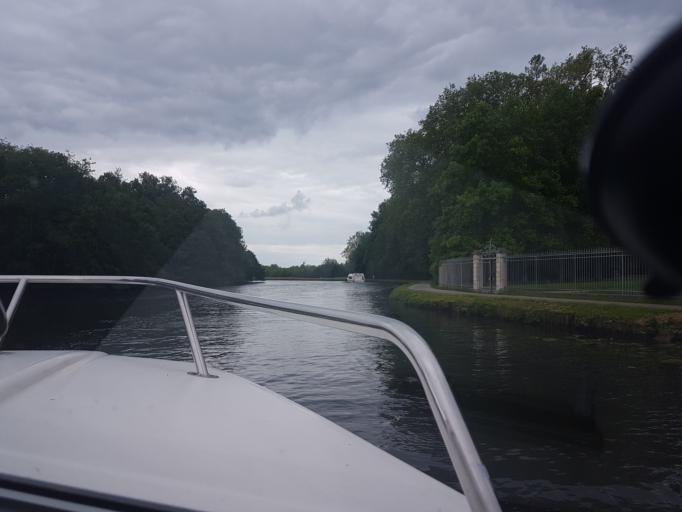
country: FR
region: Bourgogne
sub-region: Departement de l'Yonne
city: Champs-sur-Yonne
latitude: 47.7280
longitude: 3.6071
